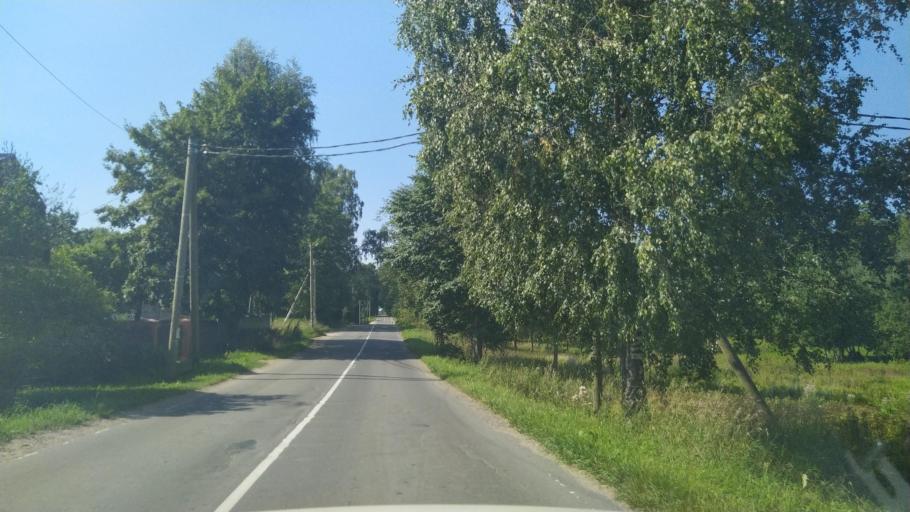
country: RU
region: Leningrad
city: Siverskiy
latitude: 59.2934
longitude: 30.0688
